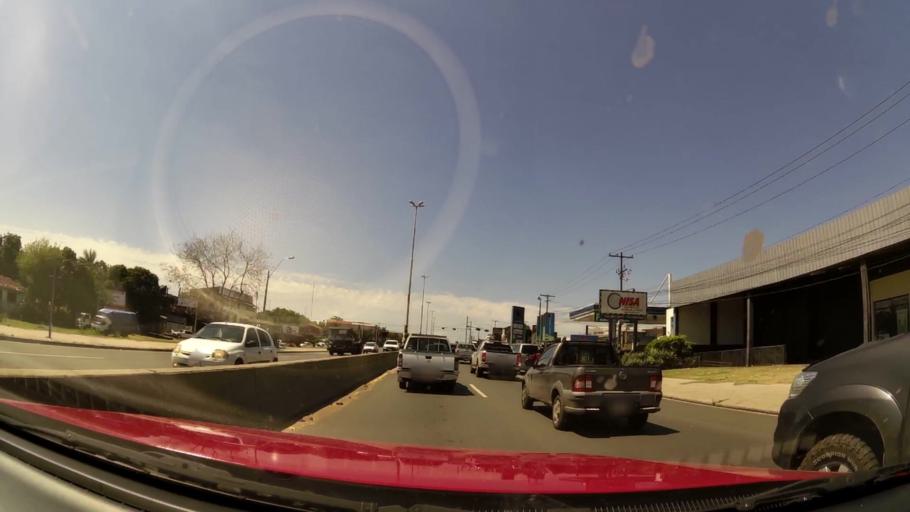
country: PY
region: Central
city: Colonia Mariano Roque Alonso
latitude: -25.2475
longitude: -57.5504
